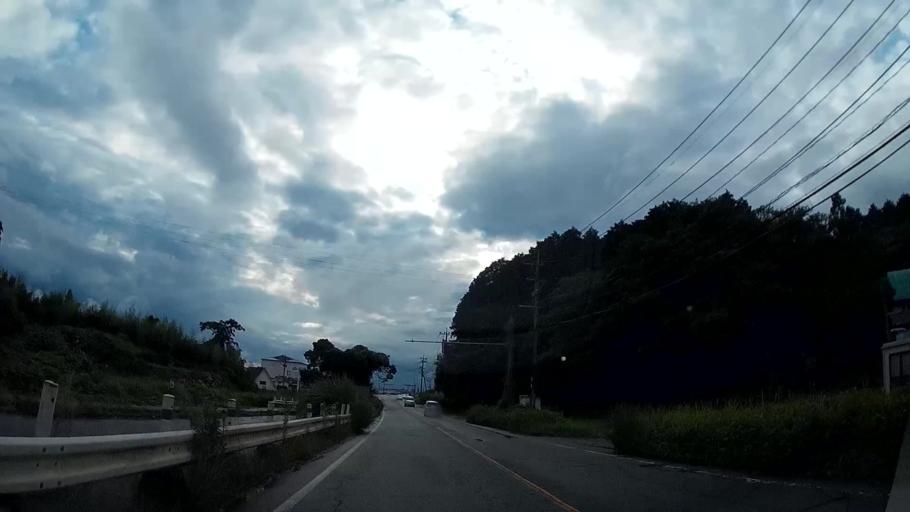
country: JP
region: Kumamoto
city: Ozu
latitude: 32.8796
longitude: 130.9074
